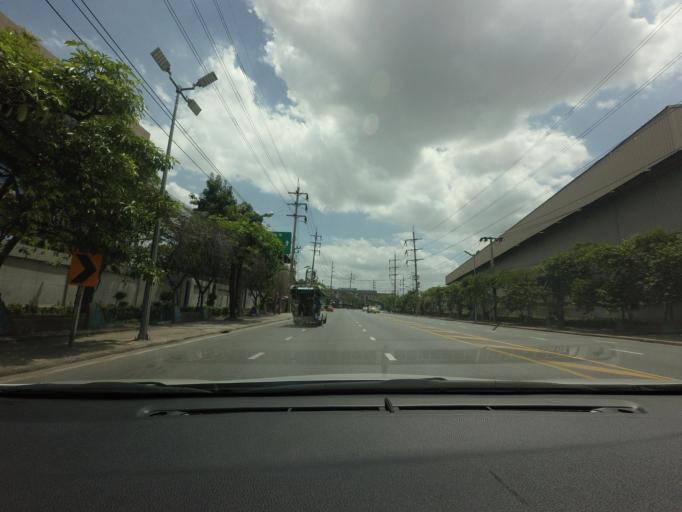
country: TH
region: Samut Prakan
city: Phra Pradaeng
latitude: 13.6508
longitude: 100.5516
